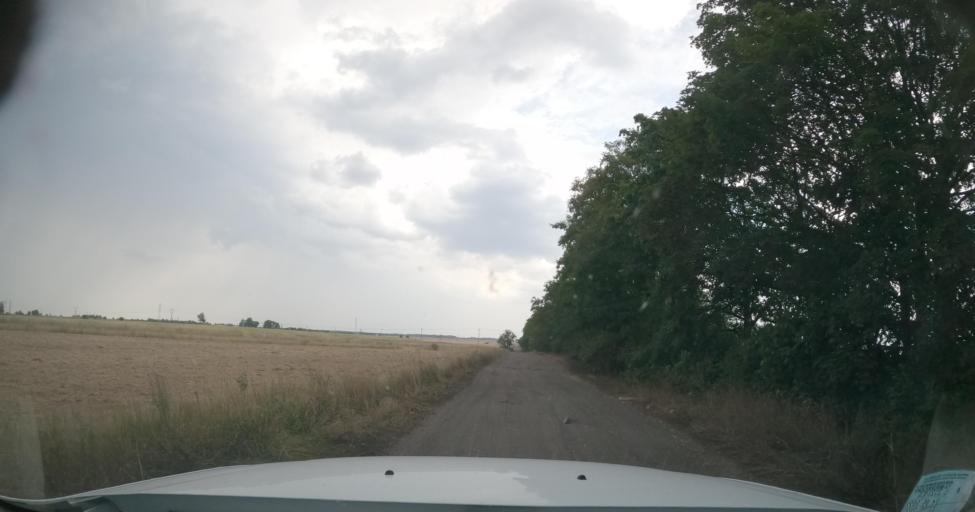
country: PL
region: West Pomeranian Voivodeship
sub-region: Powiat stargardzki
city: Stargard Szczecinski
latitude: 53.3495
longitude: 15.0641
